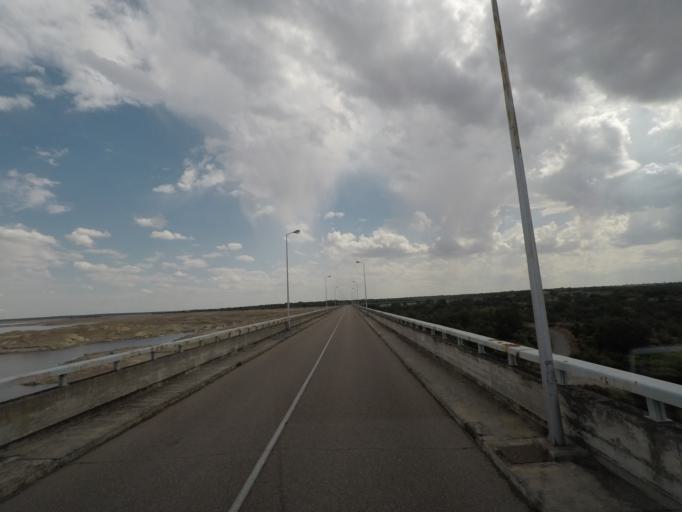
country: ES
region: Castille and Leon
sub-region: Provincia de Salamanca
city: Almendra
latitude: 41.2647
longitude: -6.3232
